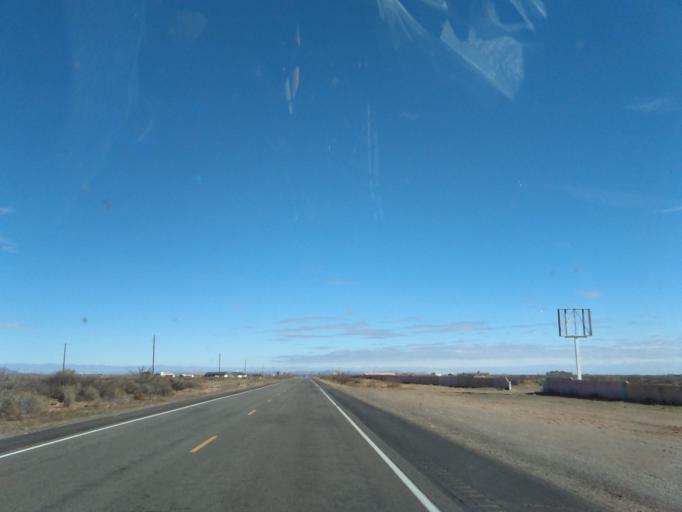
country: US
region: New Mexico
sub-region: Luna County
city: Deming
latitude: 32.2945
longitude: -107.7337
